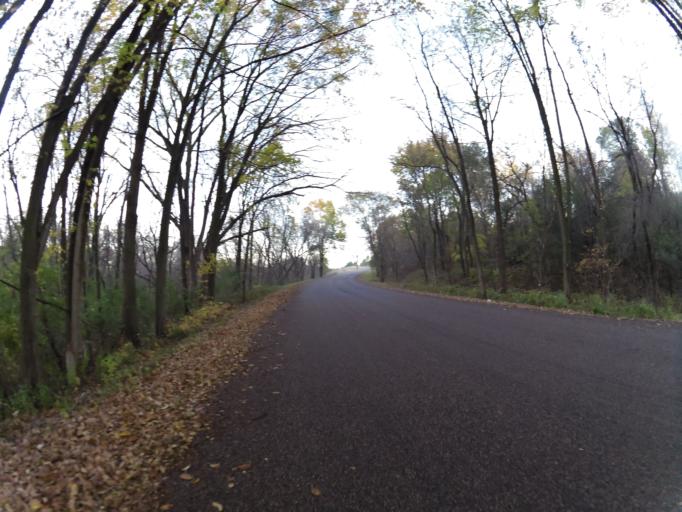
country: US
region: Minnesota
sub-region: Olmsted County
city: Rochester
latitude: 44.0444
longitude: -92.4080
